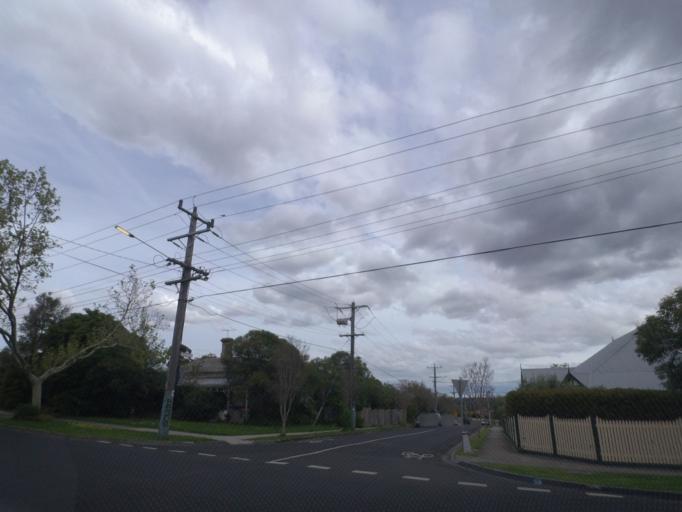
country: AU
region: Victoria
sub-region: Whitehorse
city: Box Hill
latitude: -37.8249
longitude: 145.1285
